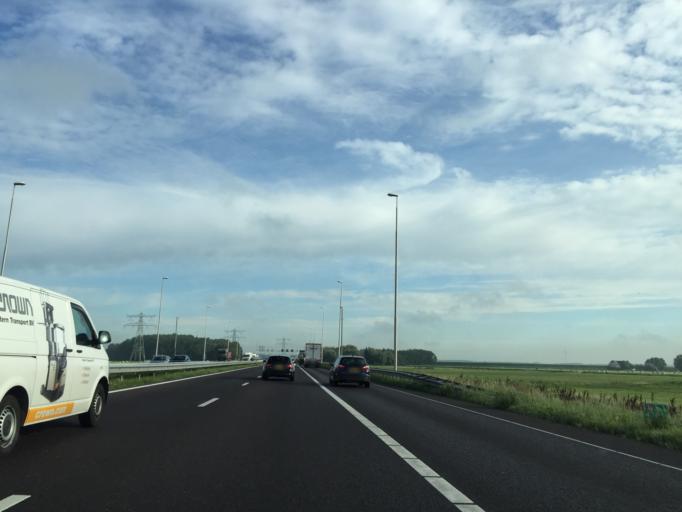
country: NL
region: North Holland
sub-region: Gemeente Haarlem
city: Haarlem
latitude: 52.3979
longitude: 4.7055
